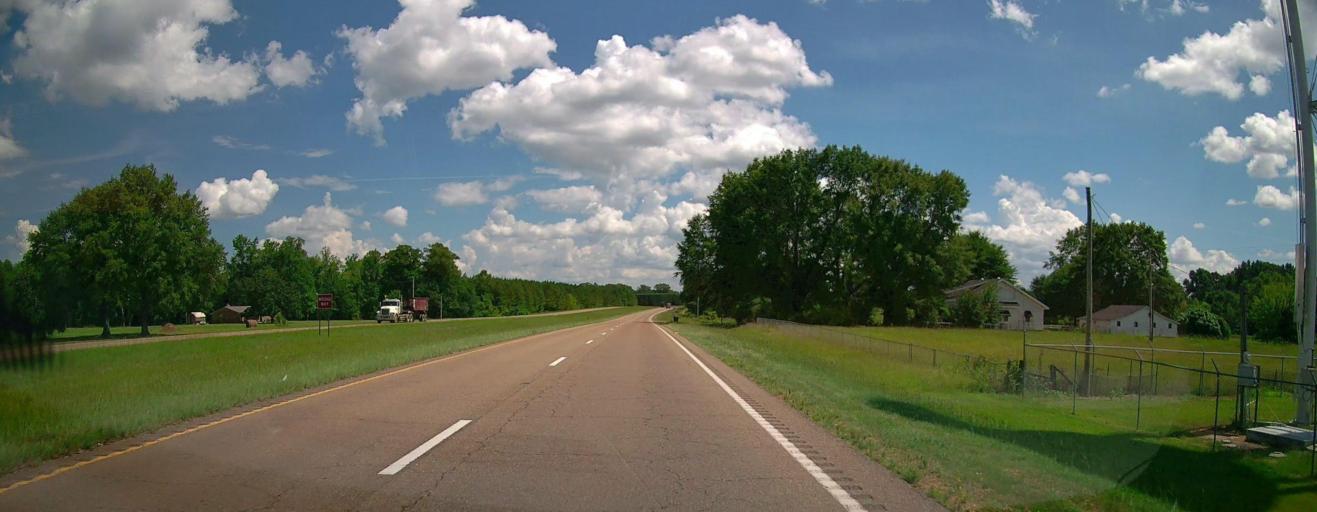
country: US
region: Mississippi
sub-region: Monroe County
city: Aberdeen
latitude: 33.7933
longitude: -88.4614
